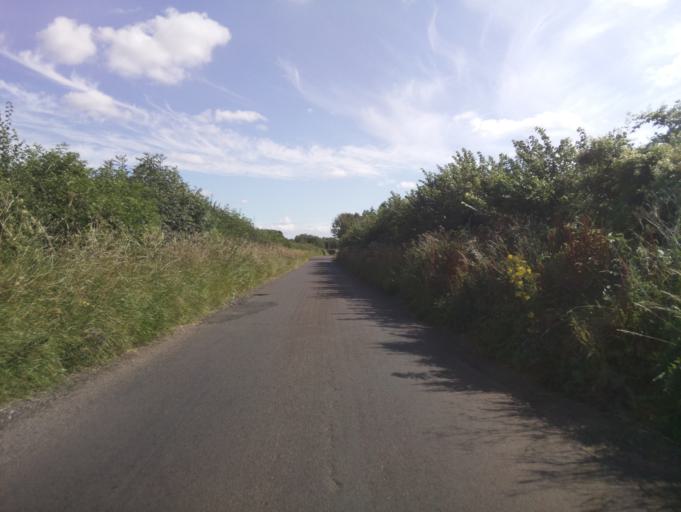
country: GB
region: England
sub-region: Gloucestershire
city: Tetbury
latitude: 51.6626
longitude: -2.1445
